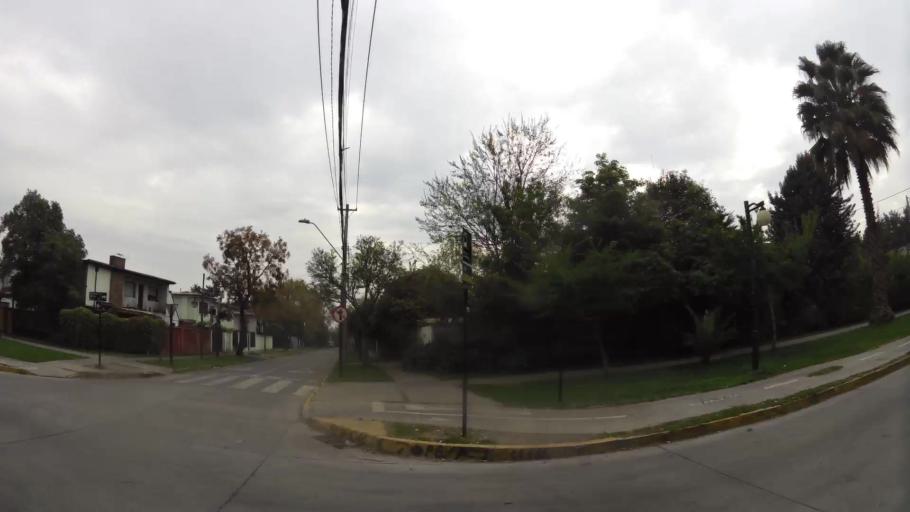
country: CL
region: Santiago Metropolitan
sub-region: Provincia de Santiago
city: Villa Presidente Frei, Nunoa, Santiago, Chile
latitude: -33.4622
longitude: -70.5876
